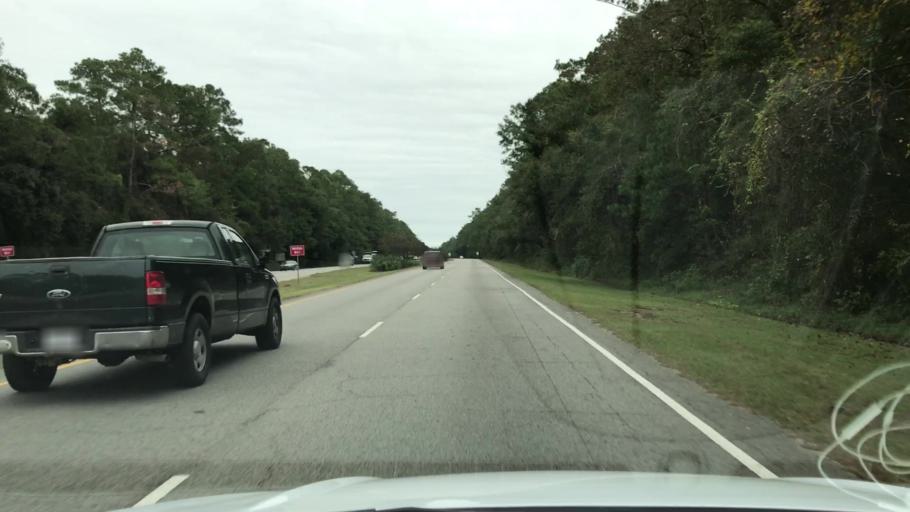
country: US
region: South Carolina
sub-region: Georgetown County
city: Murrells Inlet
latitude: 33.4966
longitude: -79.0858
